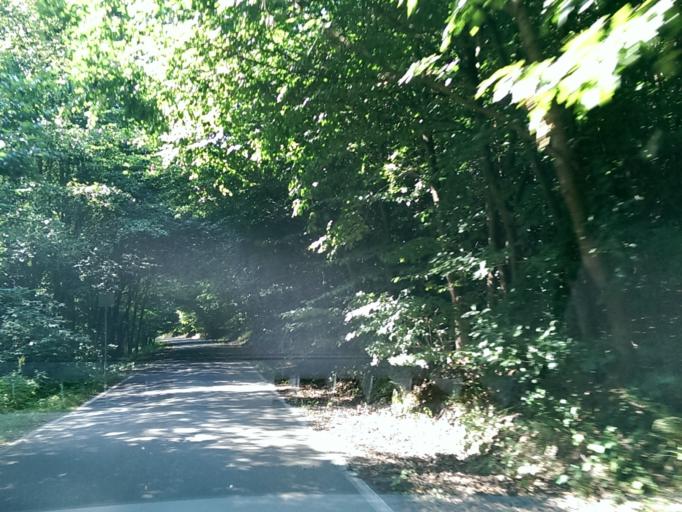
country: CZ
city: Duba
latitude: 50.4986
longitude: 14.4964
